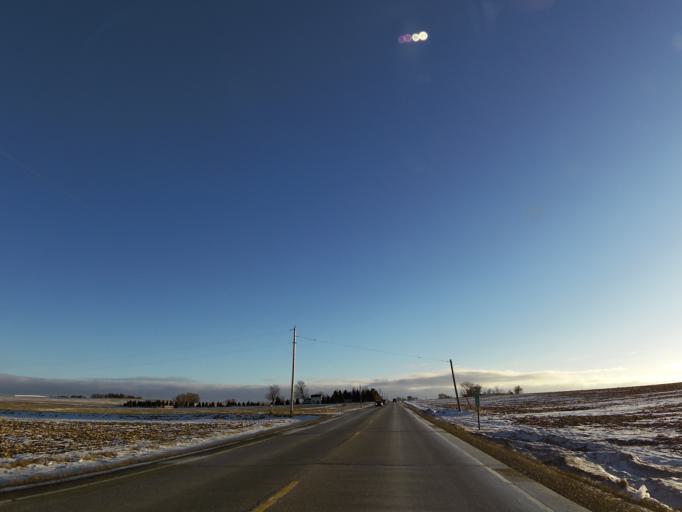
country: US
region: Minnesota
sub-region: Washington County
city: Cottage Grove
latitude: 44.8403
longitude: -92.8627
